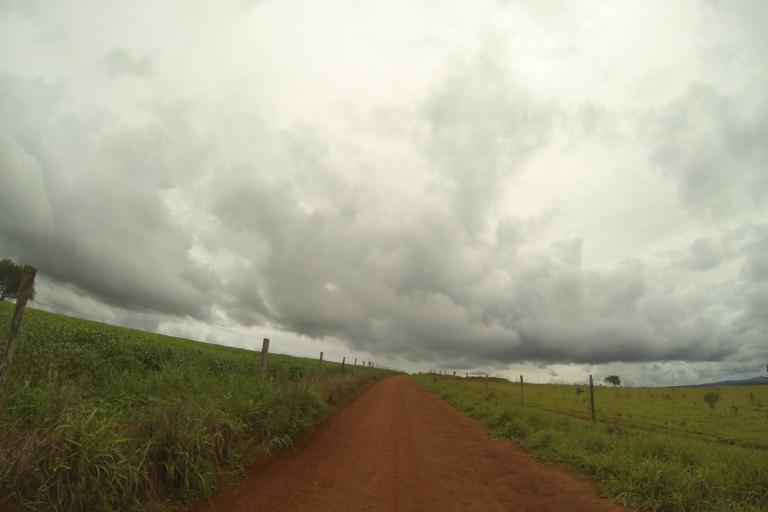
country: BR
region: Minas Gerais
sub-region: Ibia
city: Ibia
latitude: -19.7154
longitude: -46.5765
